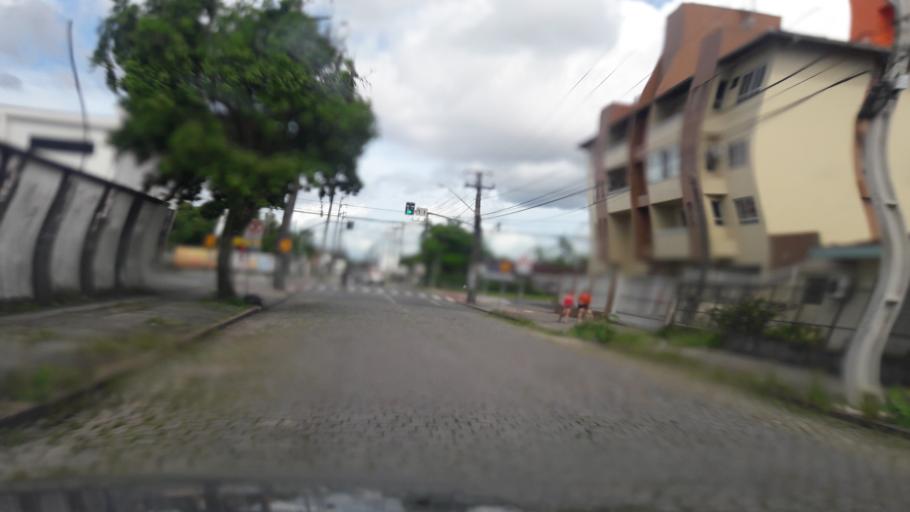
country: BR
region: Santa Catarina
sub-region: Joinville
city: Joinville
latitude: -26.3190
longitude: -48.8431
